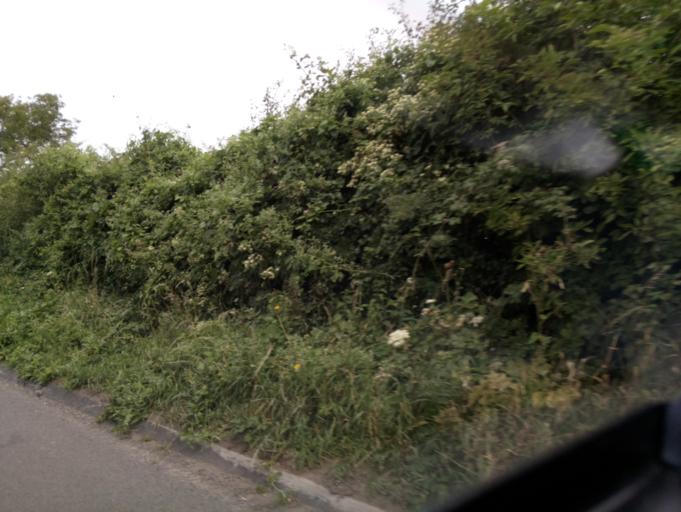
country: GB
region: England
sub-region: North Somerset
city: Kenn
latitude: 51.4090
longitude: -2.8450
